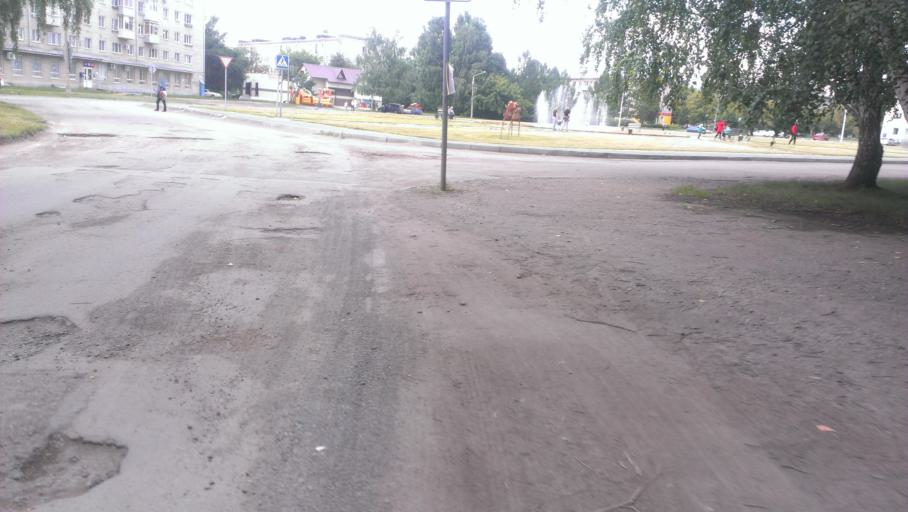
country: RU
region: Altai Krai
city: Yuzhnyy
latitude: 53.2535
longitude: 83.6927
